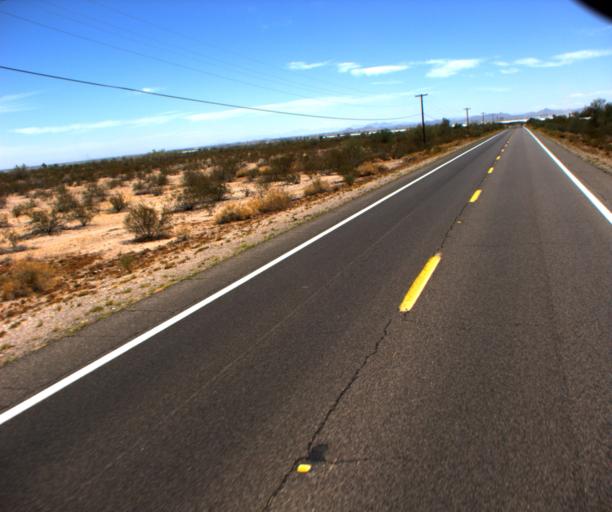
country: US
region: Arizona
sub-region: Pinal County
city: Maricopa
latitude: 32.8713
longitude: -112.0559
